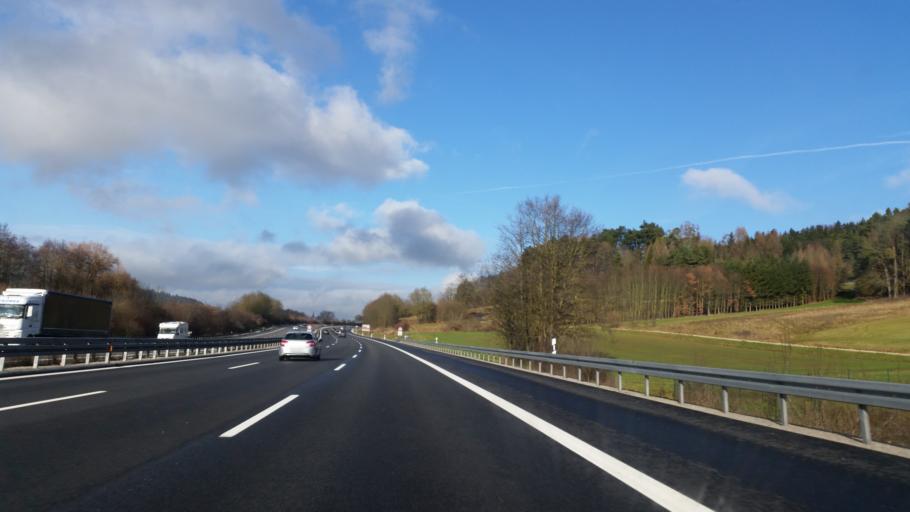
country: DE
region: Bavaria
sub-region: Regierungsbezirk Mittelfranken
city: Thalmassing
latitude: 49.1058
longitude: 11.2831
